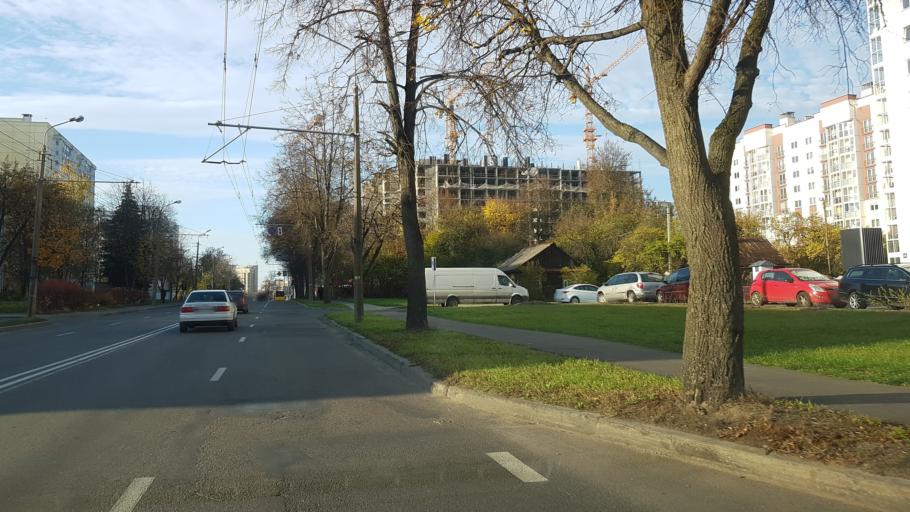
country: BY
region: Minsk
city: Minsk
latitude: 53.8821
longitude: 27.5197
